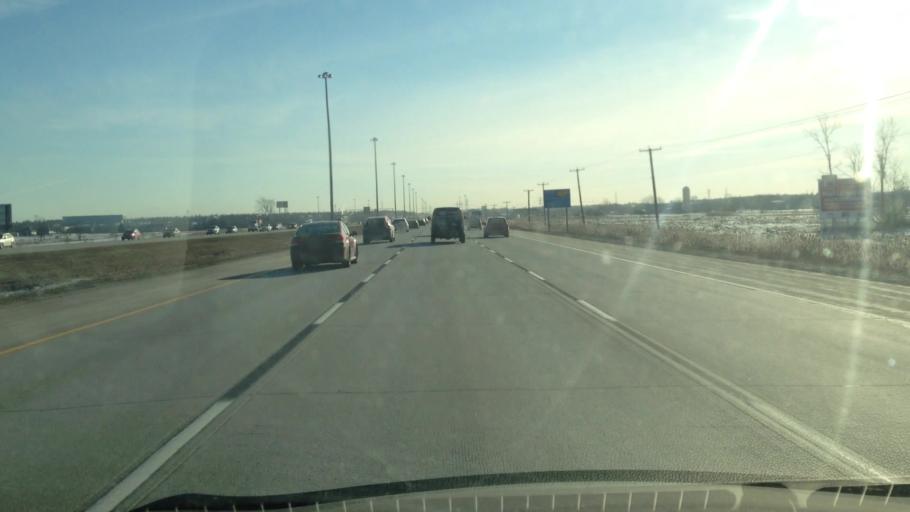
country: CA
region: Quebec
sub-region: Laurentides
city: Blainville
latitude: 45.7002
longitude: -73.9491
